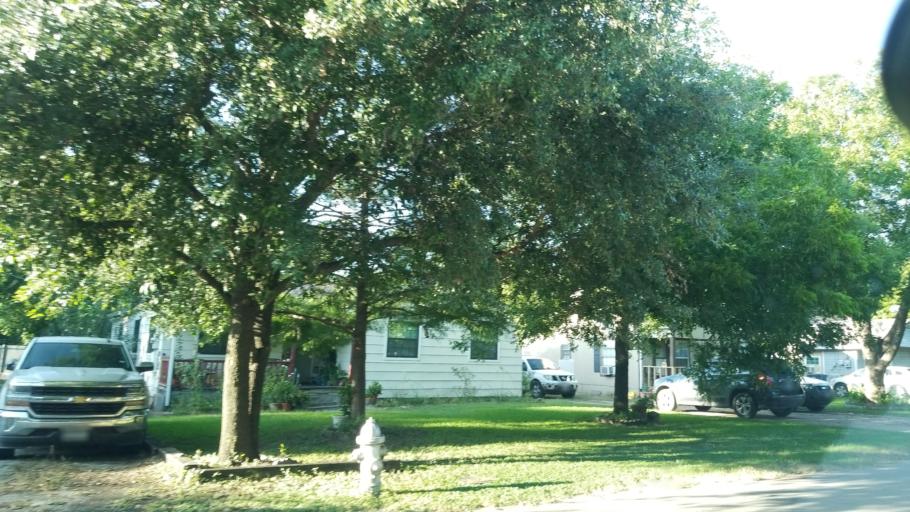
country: US
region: Texas
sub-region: Dallas County
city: Balch Springs
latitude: 32.7756
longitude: -96.6987
